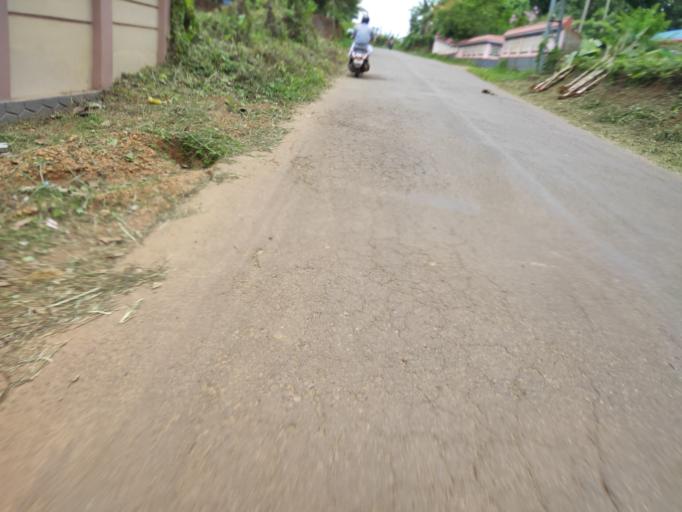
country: IN
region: Kerala
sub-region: Malappuram
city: Manjeri
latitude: 11.2393
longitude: 76.2864
